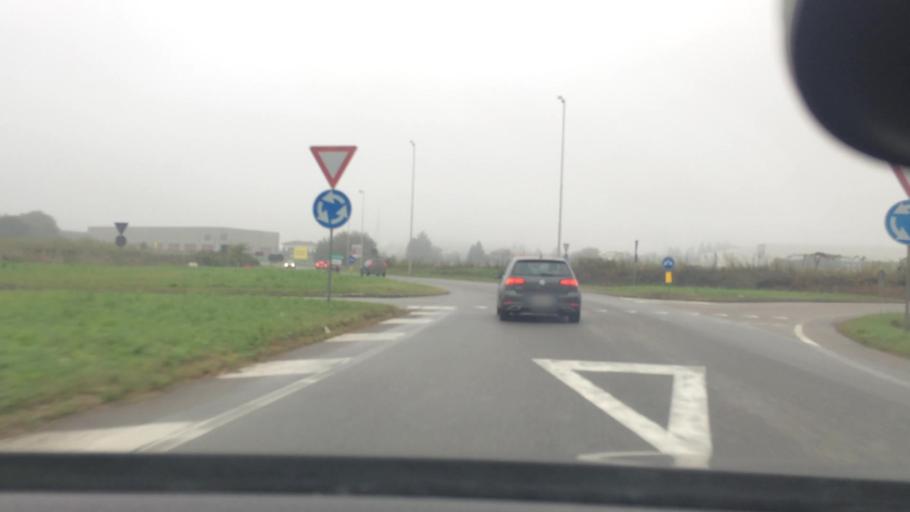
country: IT
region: Lombardy
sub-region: Provincia di Como
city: Carimate
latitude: 45.6934
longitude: 9.1019
